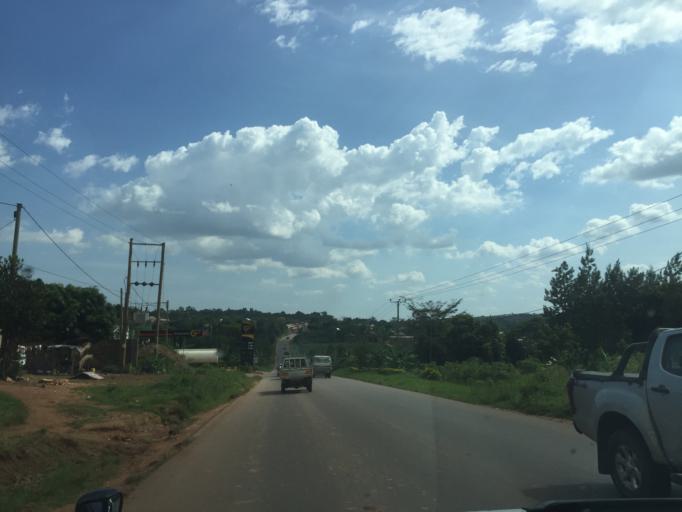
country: UG
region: Central Region
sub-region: Wakiso District
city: Wakiso
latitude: 0.5176
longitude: 32.5270
